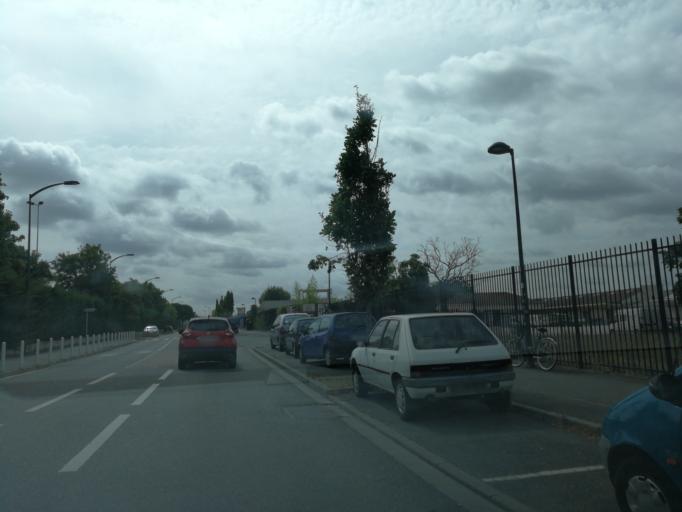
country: FR
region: Midi-Pyrenees
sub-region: Departement de la Haute-Garonne
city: Balma
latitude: 43.6239
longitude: 1.4867
